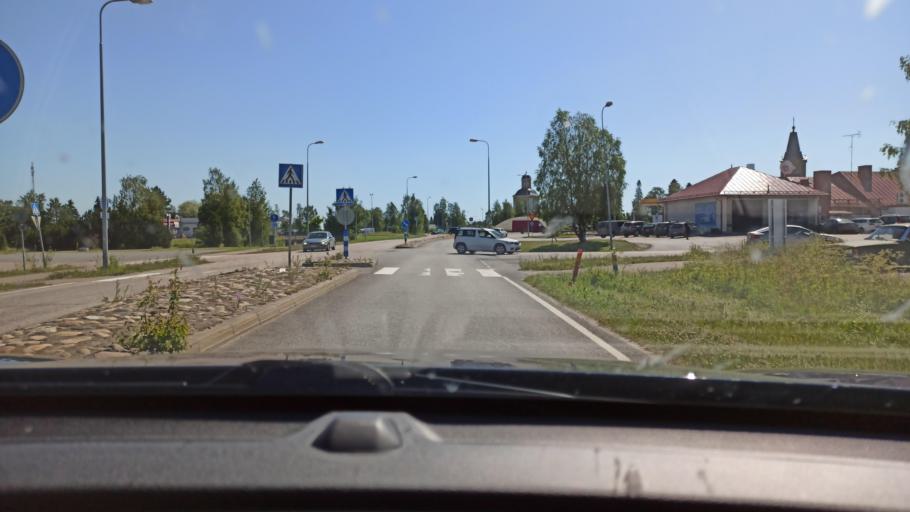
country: FI
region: Northern Ostrobothnia
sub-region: Ylivieska
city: Kalajoki
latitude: 64.2569
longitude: 23.9355
